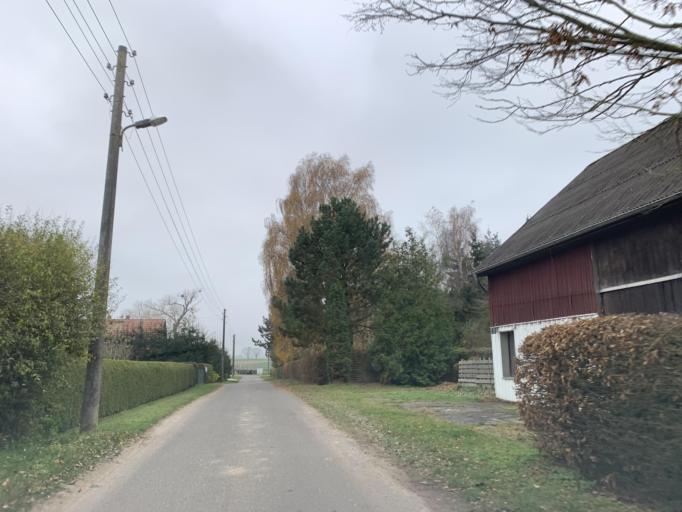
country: DE
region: Mecklenburg-Vorpommern
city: Blankensee
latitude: 53.3997
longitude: 13.2891
